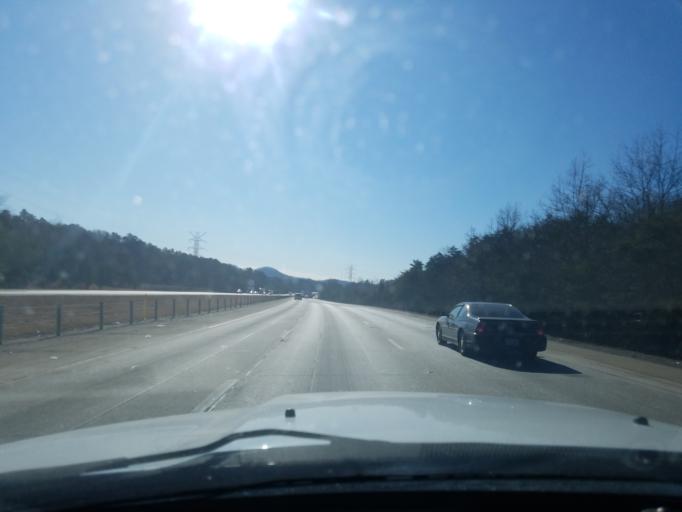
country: US
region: Kentucky
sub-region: Bullitt County
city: Lebanon Junction
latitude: 37.8792
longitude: -85.7023
